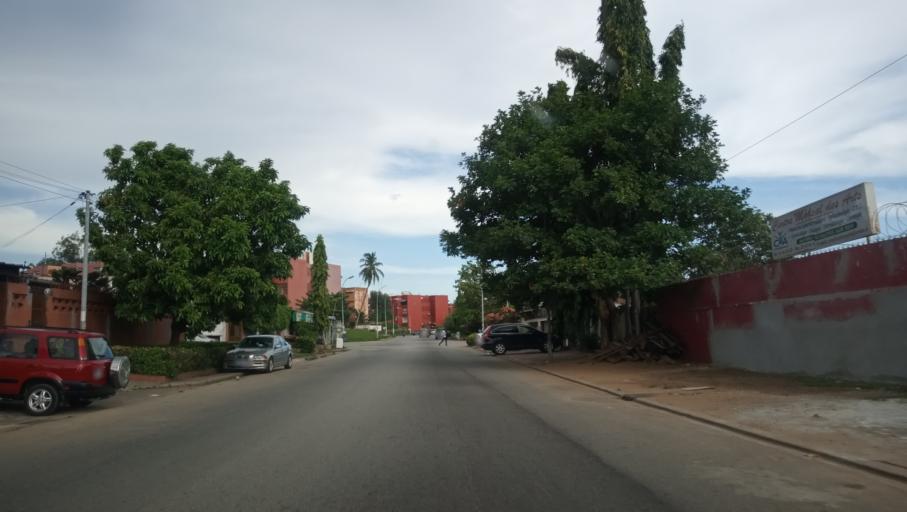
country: CI
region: Lagunes
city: Abidjan
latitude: 5.3442
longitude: -3.9800
